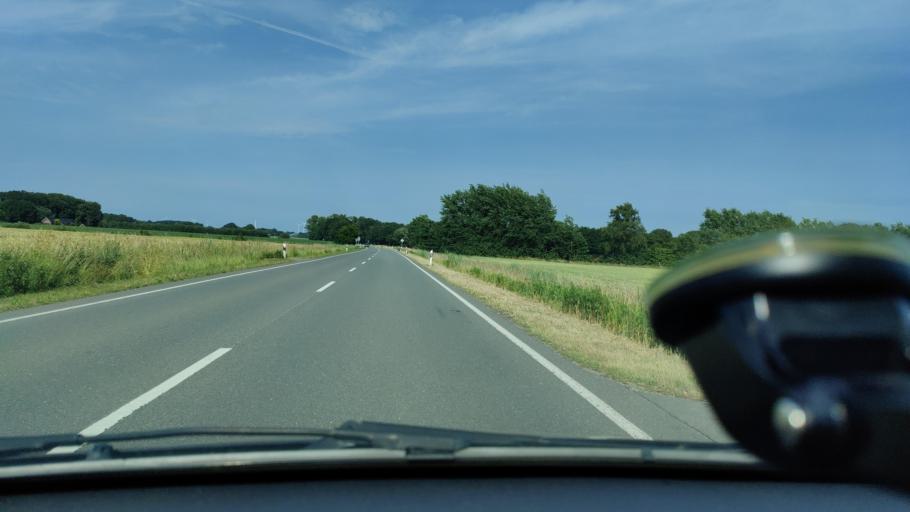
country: DE
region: North Rhine-Westphalia
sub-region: Regierungsbezirk Munster
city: Legden
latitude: 51.9745
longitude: 7.0878
